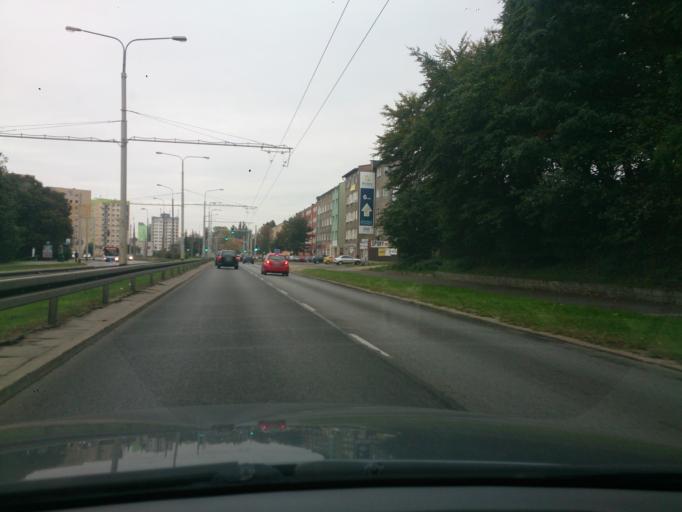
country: PL
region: Pomeranian Voivodeship
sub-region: Gdynia
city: Pogorze
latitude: 54.5367
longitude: 18.4764
